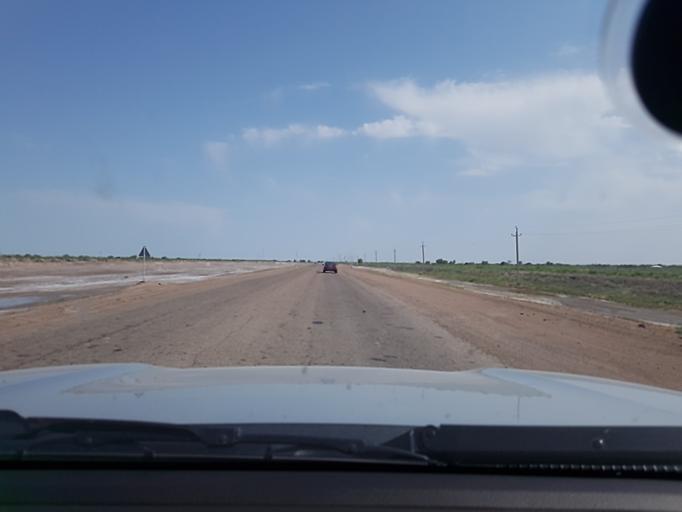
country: TM
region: Dasoguz
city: Boldumsaz
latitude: 42.1848
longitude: 59.5661
